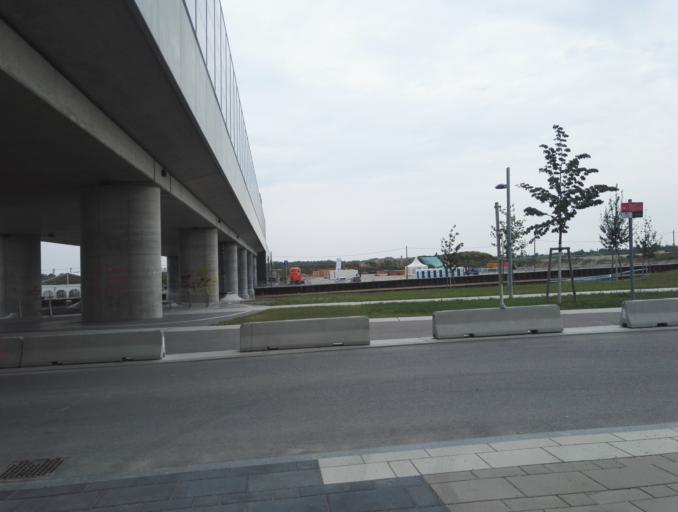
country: AT
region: Lower Austria
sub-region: Politischer Bezirk Ganserndorf
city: Gross-Enzersdorf
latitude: 48.2256
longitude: 16.5084
